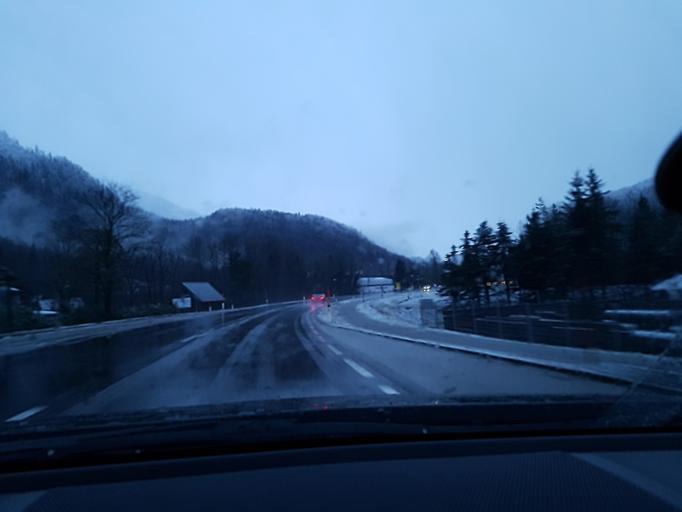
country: AT
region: Upper Austria
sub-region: Politischer Bezirk Gmunden
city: Bad Ischl
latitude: 47.6864
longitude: 13.6262
